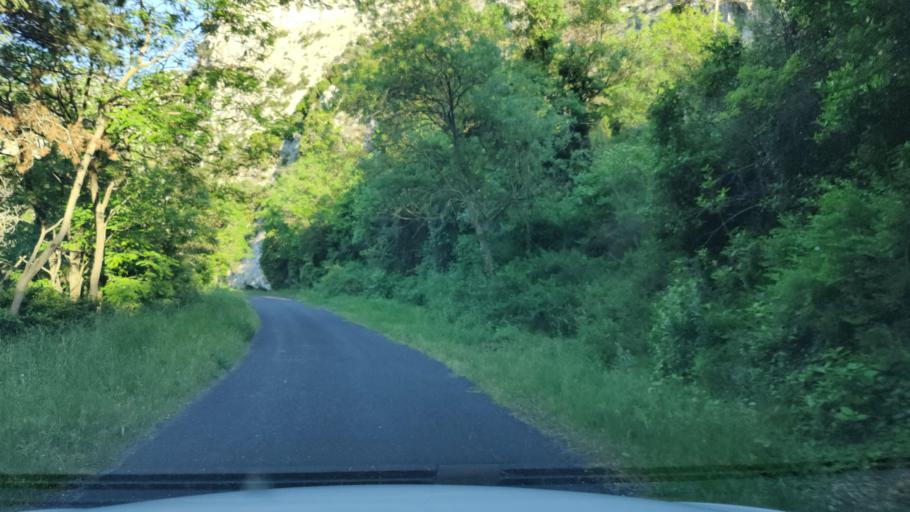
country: FR
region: Languedoc-Roussillon
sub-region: Departement des Pyrenees-Orientales
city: Estagel
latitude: 42.8072
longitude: 2.7416
